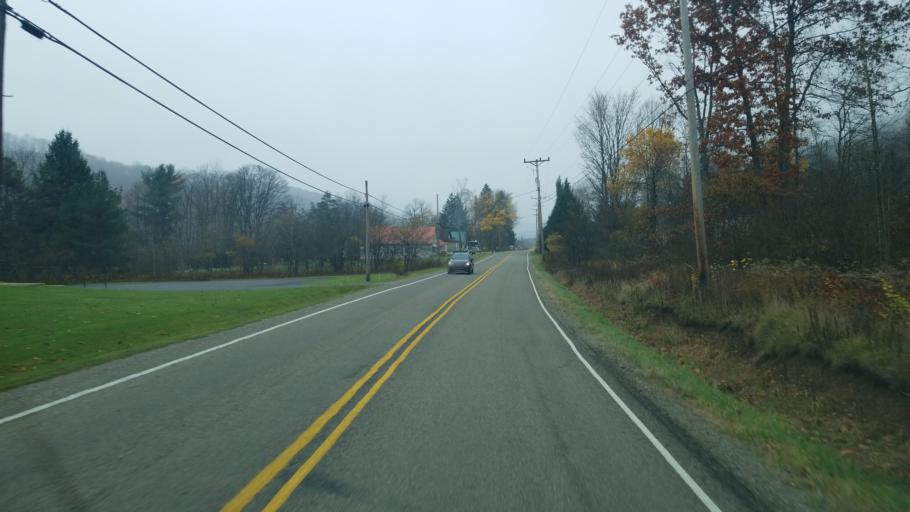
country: US
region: Pennsylvania
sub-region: McKean County
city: Smethport
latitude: 41.8859
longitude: -78.4968
